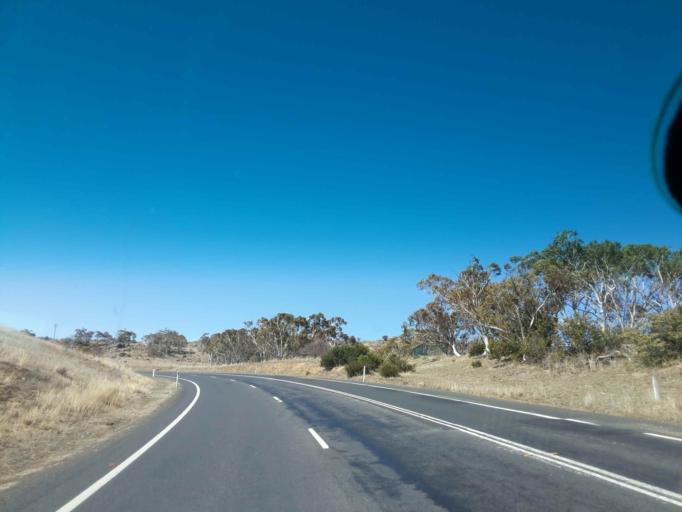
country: AU
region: New South Wales
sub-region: Snowy River
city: Jindabyne
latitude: -36.4140
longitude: 148.5968
